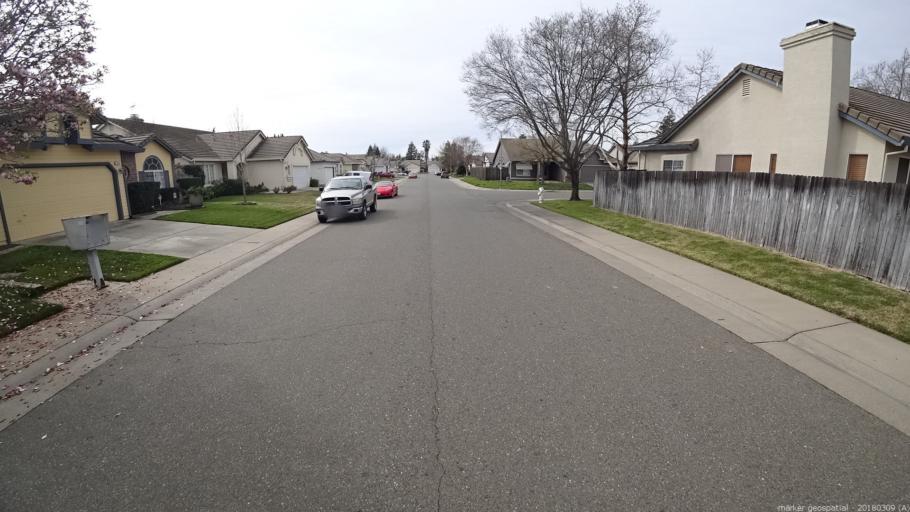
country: US
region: California
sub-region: Sacramento County
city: Vineyard
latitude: 38.4611
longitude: -121.3673
